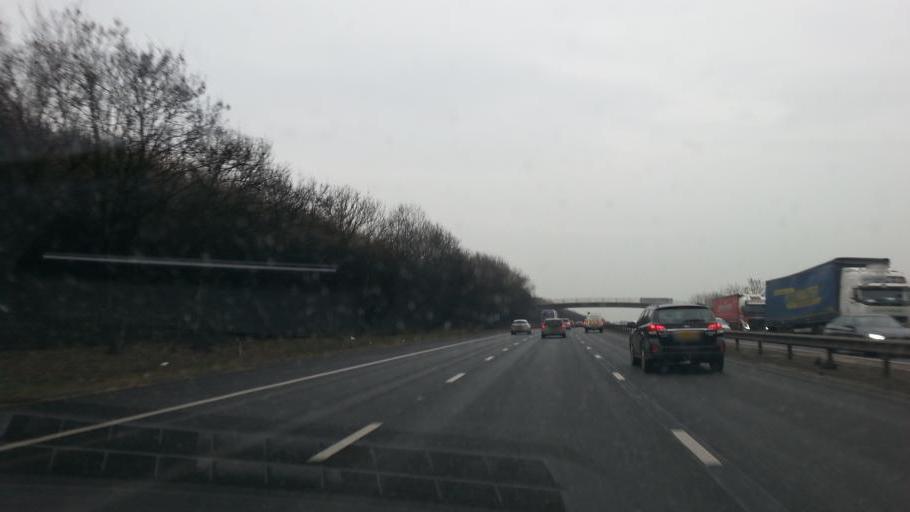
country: GB
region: England
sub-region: Essex
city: Harlow
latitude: 51.7605
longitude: 0.1488
